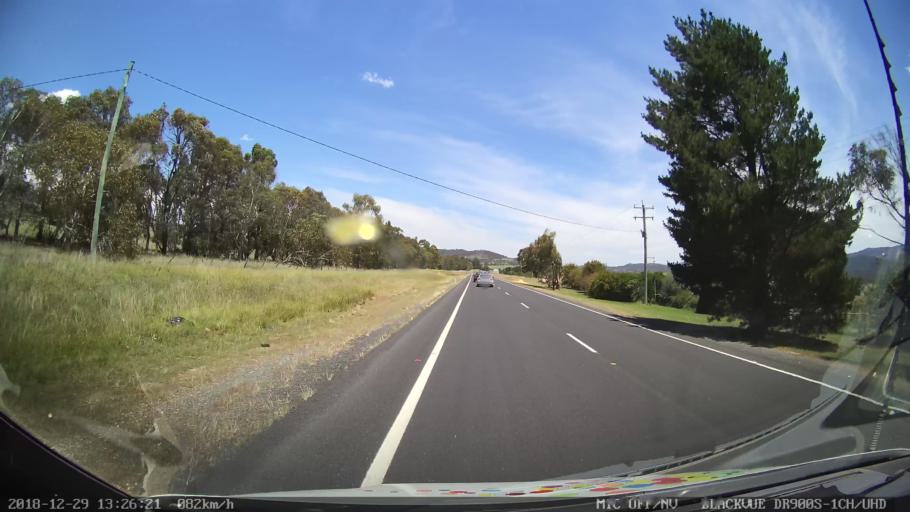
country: AU
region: New South Wales
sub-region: Cooma-Monaro
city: Cooma
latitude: -35.8545
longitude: 149.1593
